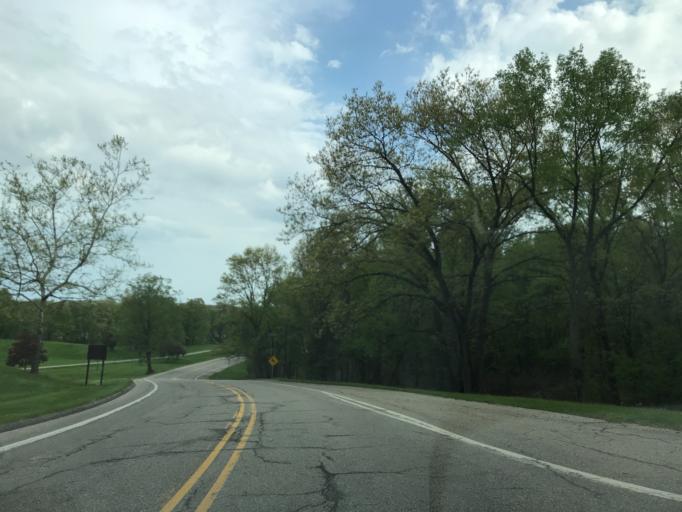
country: US
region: Michigan
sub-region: Oakland County
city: Milford
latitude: 42.5491
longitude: -83.6406
